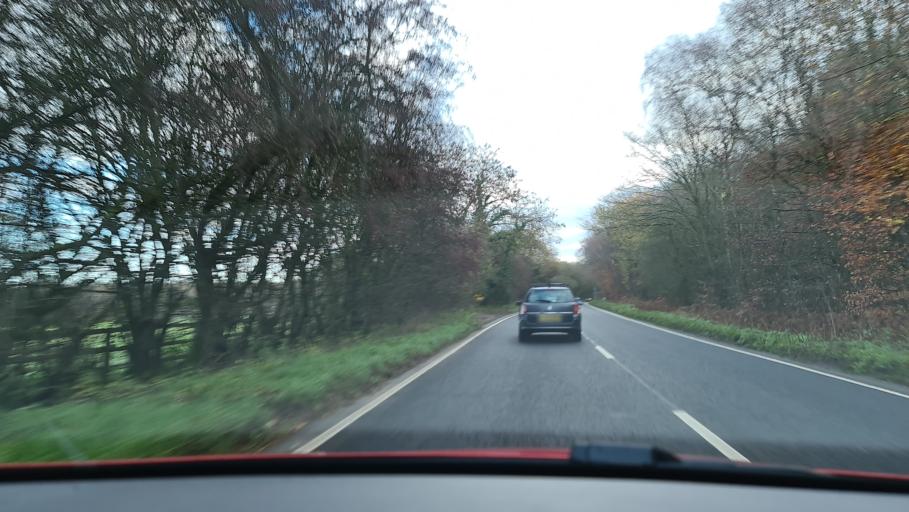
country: GB
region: England
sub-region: Buckinghamshire
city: Amersham
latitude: 51.6617
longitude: -0.6706
